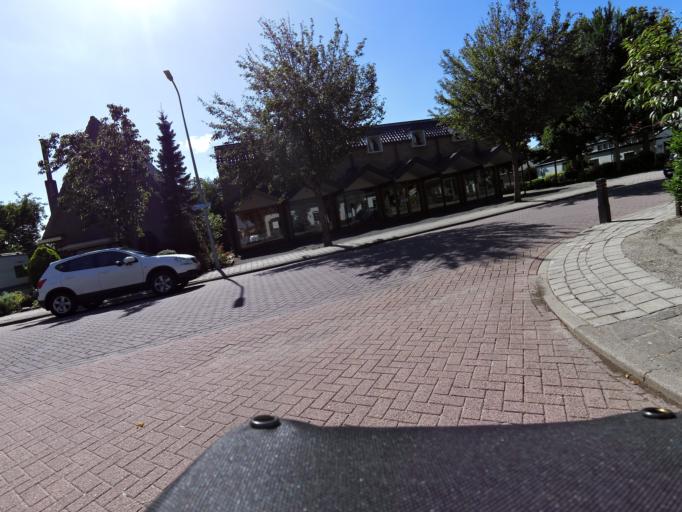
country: NL
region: South Holland
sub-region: Gemeente Goeree-Overflakkee
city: Dirksland
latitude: 51.7689
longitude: 4.0680
